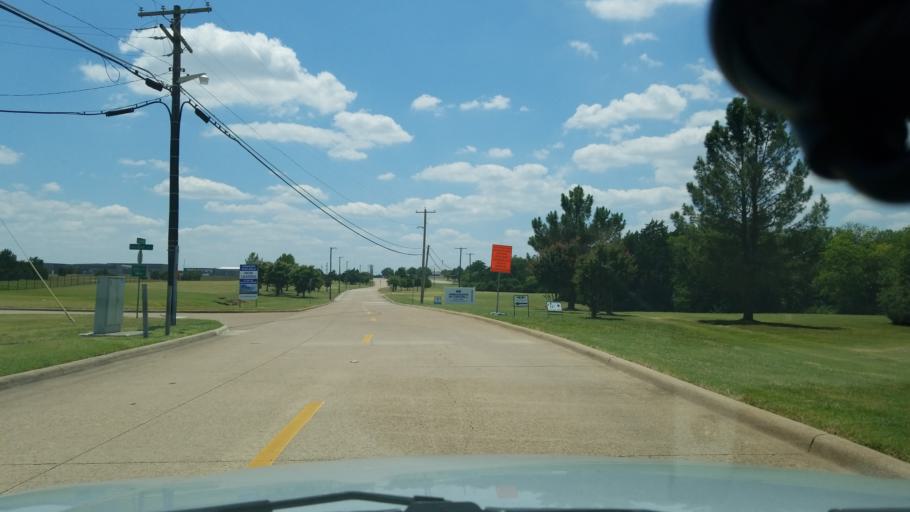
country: US
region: Texas
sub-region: Dallas County
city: Cockrell Hill
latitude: 32.6845
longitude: -96.8593
